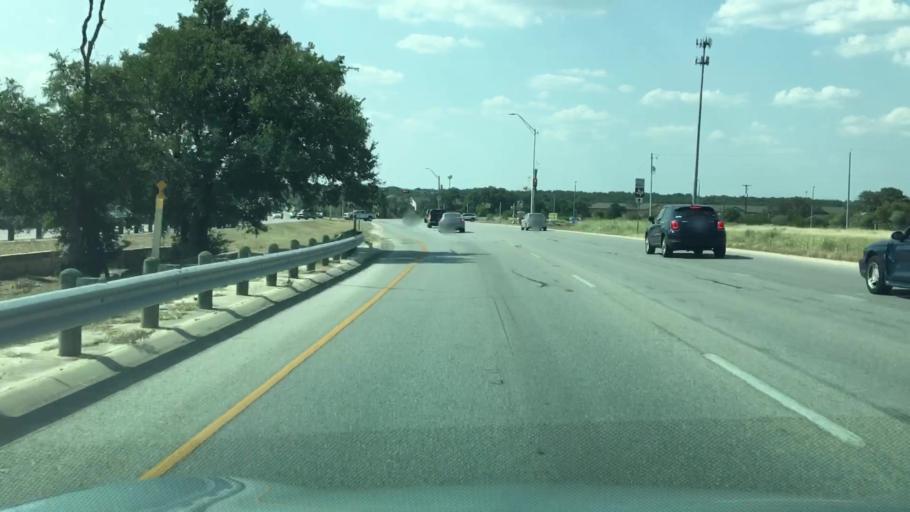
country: US
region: Texas
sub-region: Hays County
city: San Marcos
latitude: 29.8798
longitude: -97.9707
